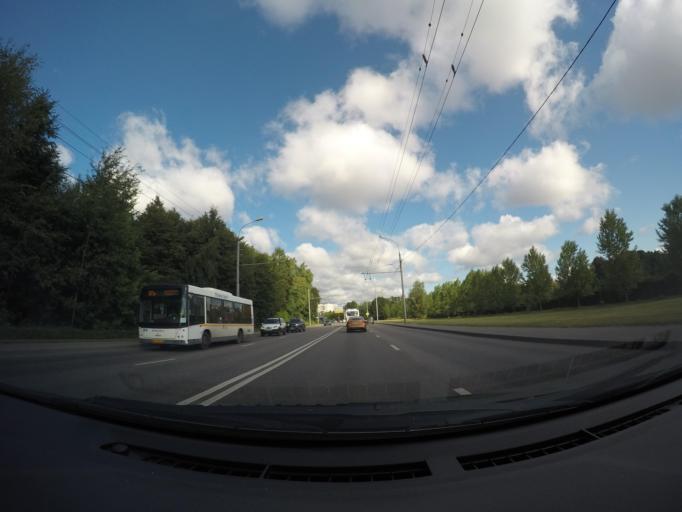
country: RU
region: Moscow
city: Khimki
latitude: 55.8730
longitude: 37.4387
